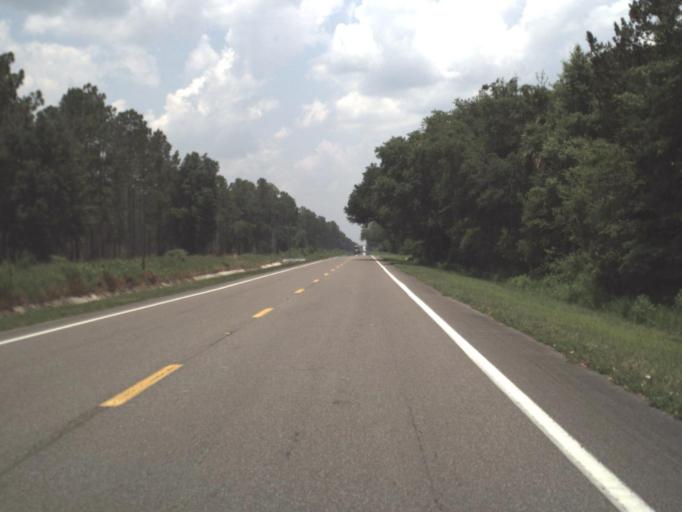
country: US
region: Florida
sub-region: Putnam County
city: Palatka
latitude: 29.4997
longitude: -81.7463
